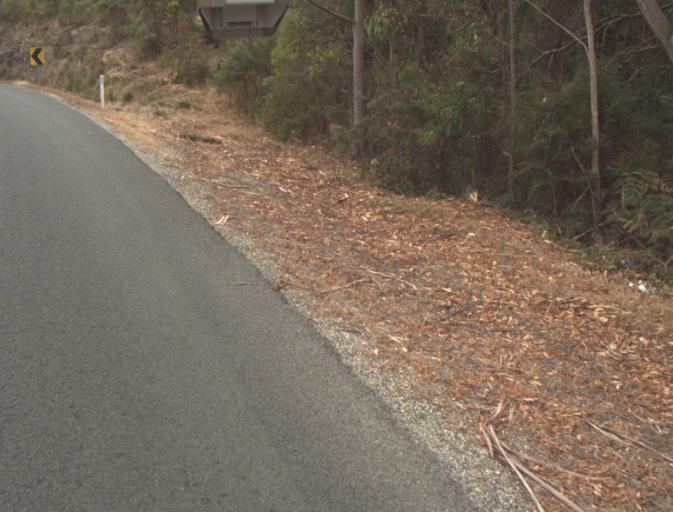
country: AU
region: Tasmania
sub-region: Dorset
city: Bridport
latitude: -41.1729
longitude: 147.2682
